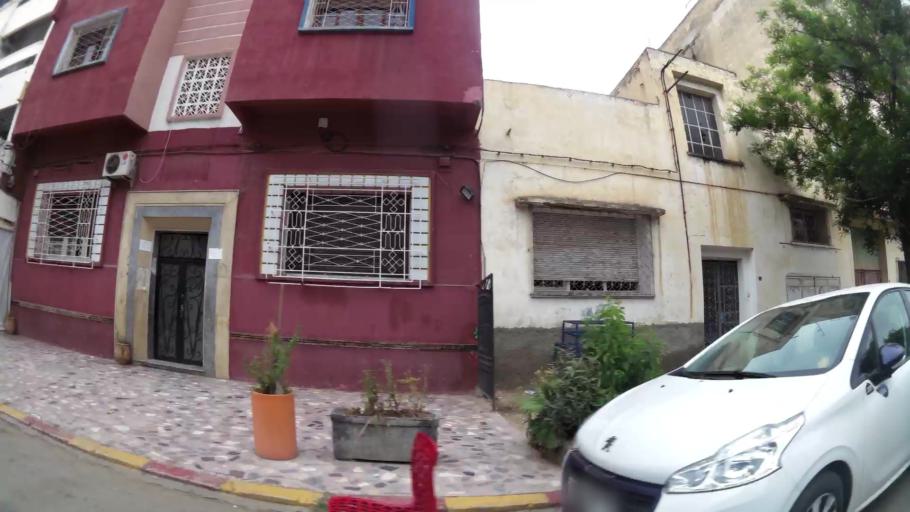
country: MA
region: Fes-Boulemane
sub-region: Fes
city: Fes
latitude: 34.0411
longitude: -5.0071
